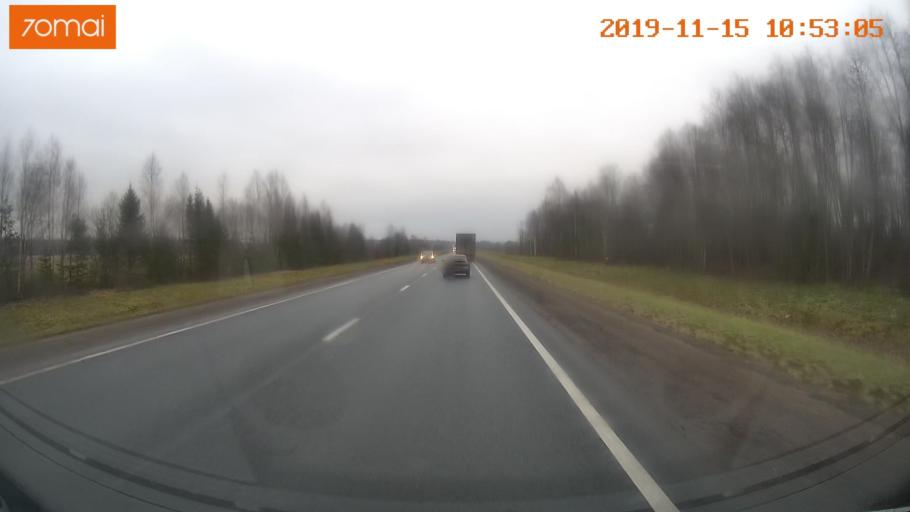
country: RU
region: Vologda
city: Chebsara
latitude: 59.1709
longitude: 38.7467
